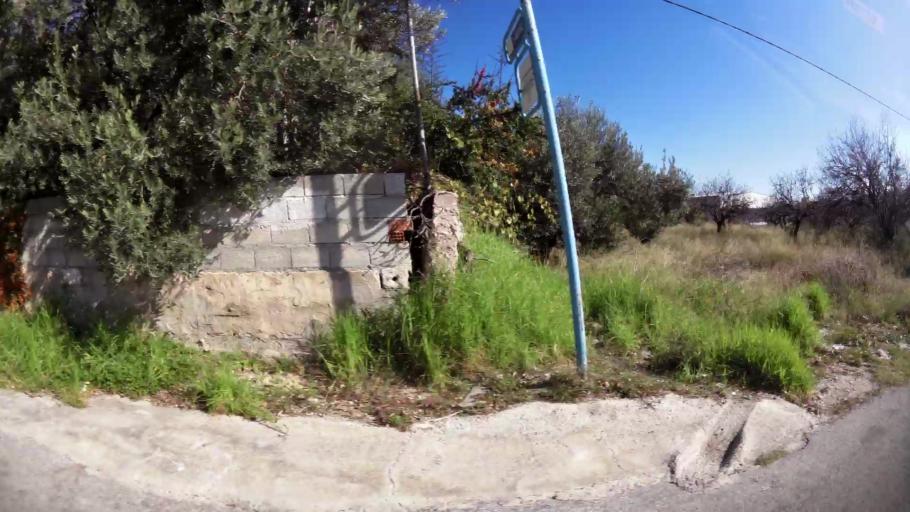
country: GR
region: Attica
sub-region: Nomarchia Anatolikis Attikis
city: Anthousa
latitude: 38.0177
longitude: 23.8724
